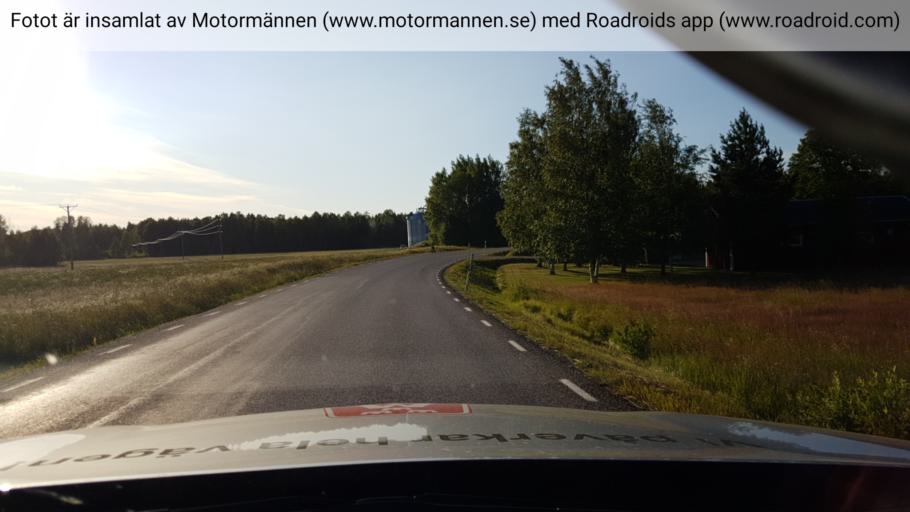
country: SE
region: Vaestmanland
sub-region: Surahammars Kommun
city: Ramnas
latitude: 59.9351
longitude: 16.2967
